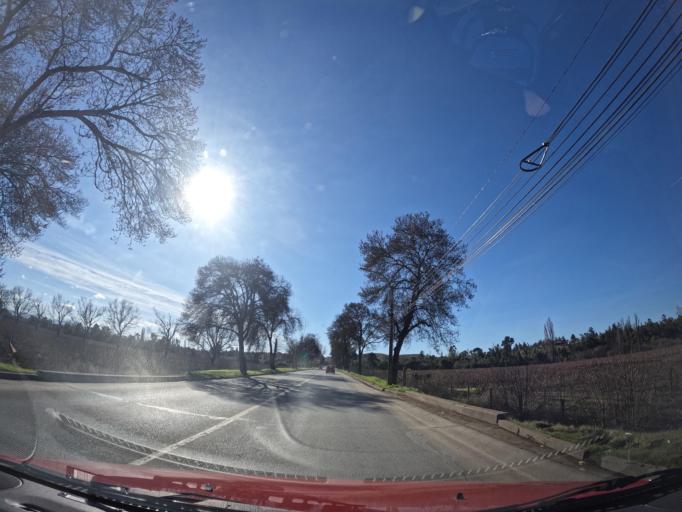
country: CL
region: Maule
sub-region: Provincia de Cauquenes
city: Cauquenes
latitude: -35.9593
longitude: -72.3118
